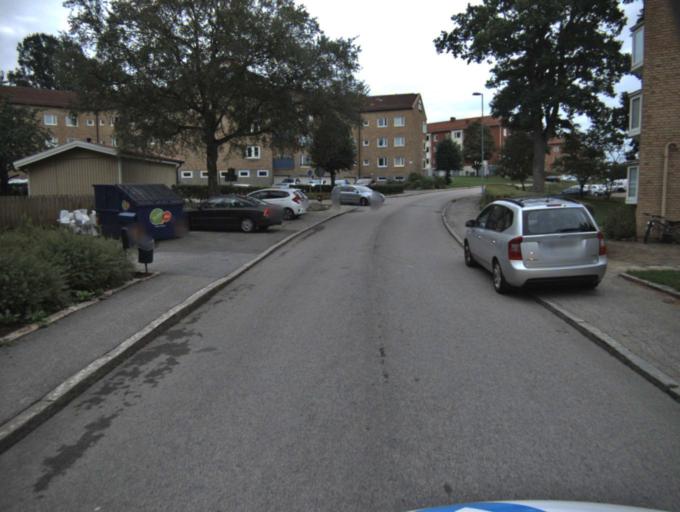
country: SE
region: Vaestra Goetaland
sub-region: Ulricehamns Kommun
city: Ulricehamn
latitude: 57.7851
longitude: 13.4152
